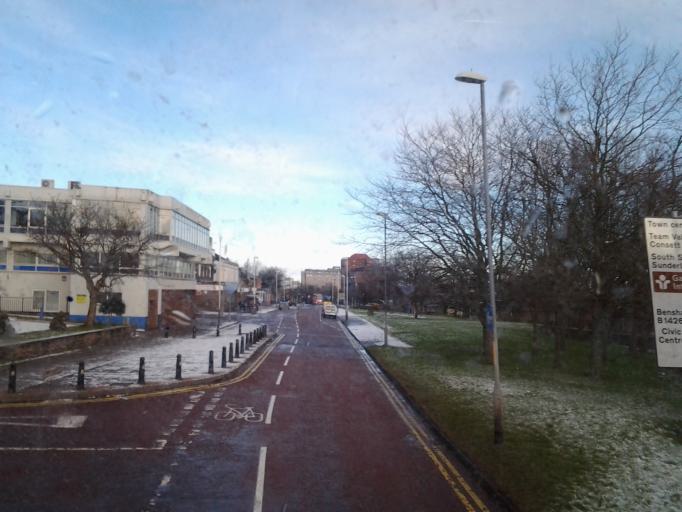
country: GB
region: England
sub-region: Gateshead
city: Gateshead
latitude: 54.9559
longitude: -1.6001
